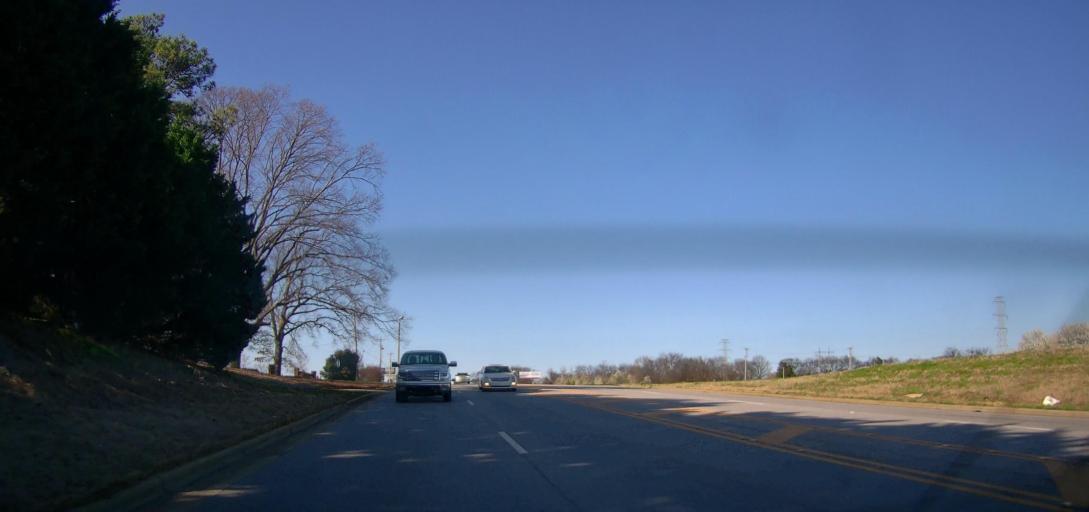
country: US
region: Alabama
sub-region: Colbert County
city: Muscle Shoals
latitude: 34.7155
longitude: -87.6350
